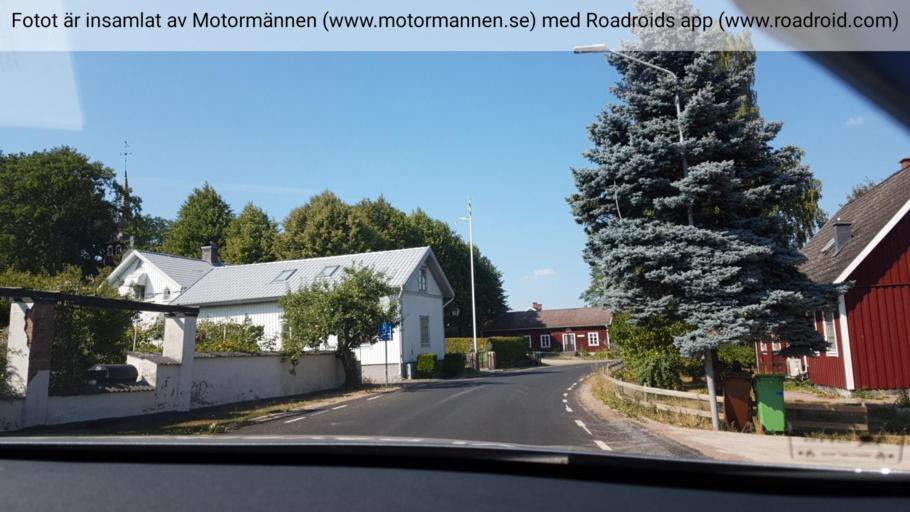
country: SE
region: Vaestra Goetaland
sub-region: Skovde Kommun
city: Stopen
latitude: 58.5822
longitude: 13.8542
